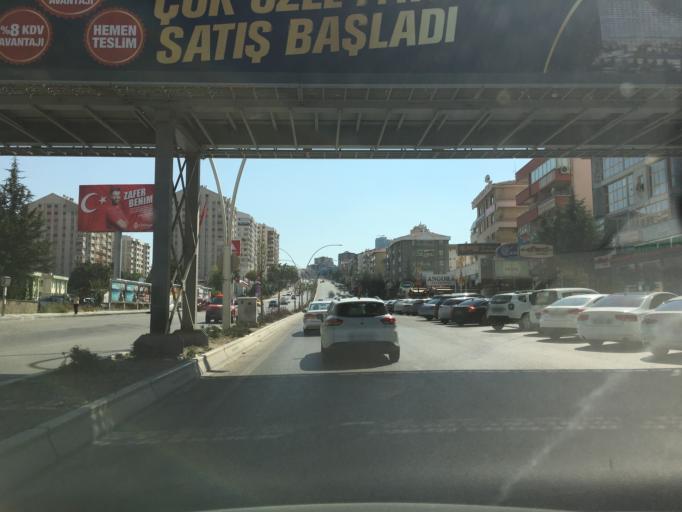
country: TR
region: Ankara
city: Cankaya
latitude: 39.8732
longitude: 32.8620
